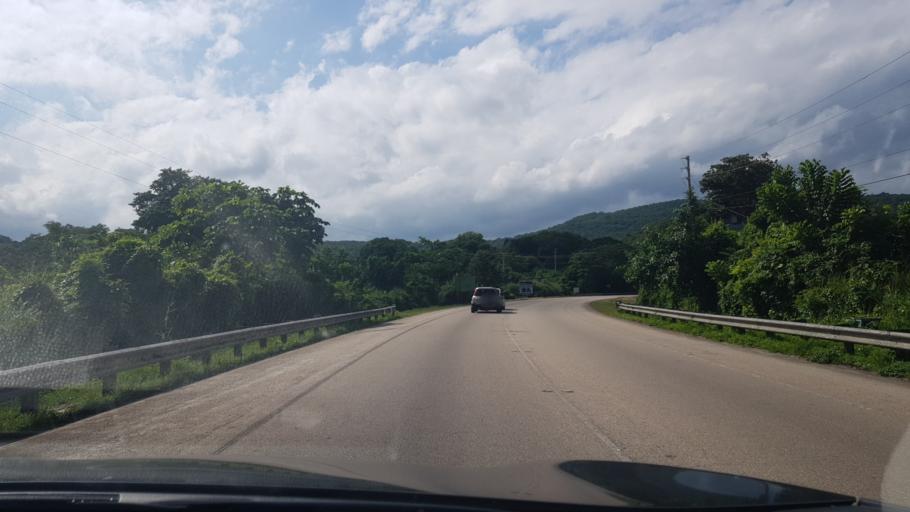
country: JM
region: Saint Ann
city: Discovery Bay
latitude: 18.4629
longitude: -77.4513
